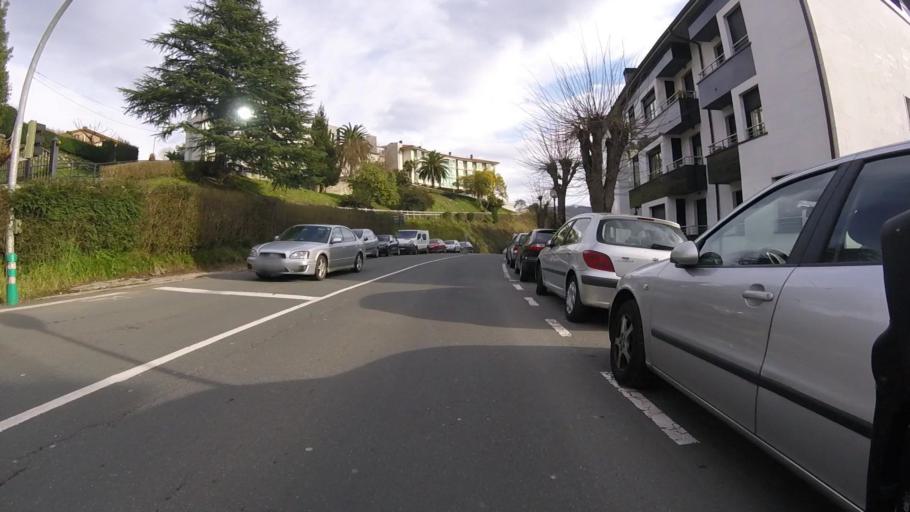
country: ES
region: Basque Country
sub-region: Provincia de Guipuzcoa
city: Lezo
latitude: 43.3001
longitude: -1.8598
